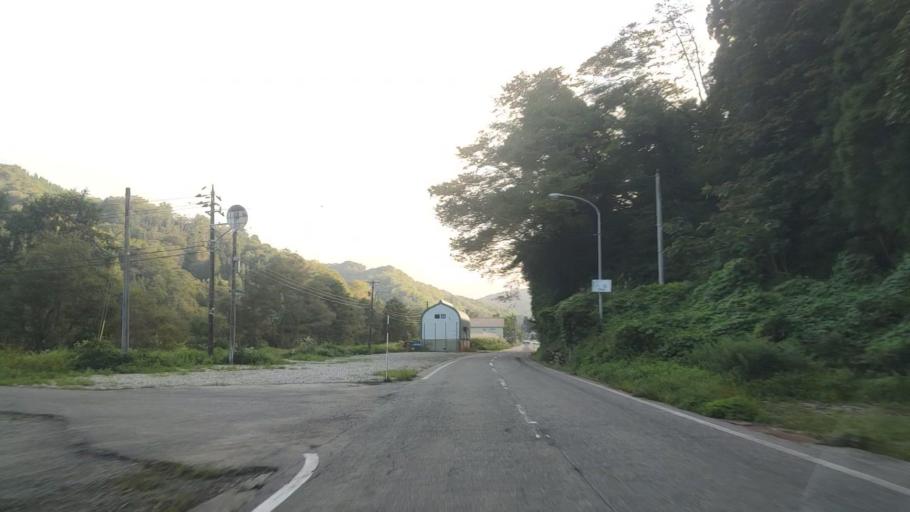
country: JP
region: Toyama
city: Yatsuomachi-higashikumisaka
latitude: 36.4607
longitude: 137.0431
